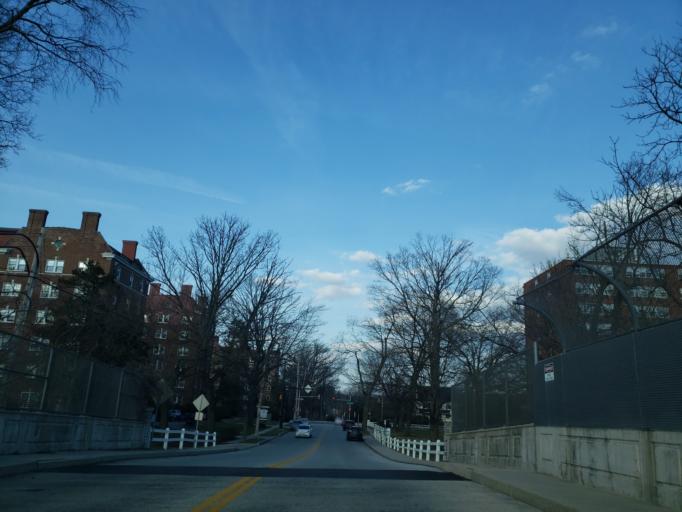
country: US
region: Pennsylvania
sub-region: Montgomery County
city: Bryn Mawr
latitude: 40.0237
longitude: -75.3197
